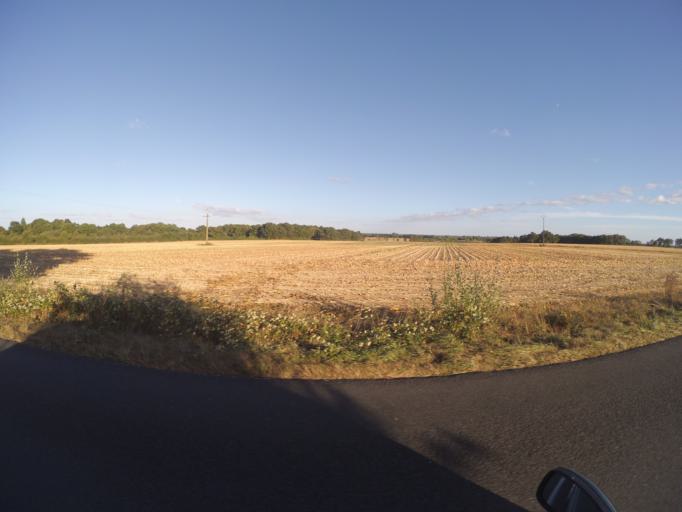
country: FR
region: Pays de la Loire
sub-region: Departement de la Loire-Atlantique
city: Remouille
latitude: 47.0660
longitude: -1.3551
